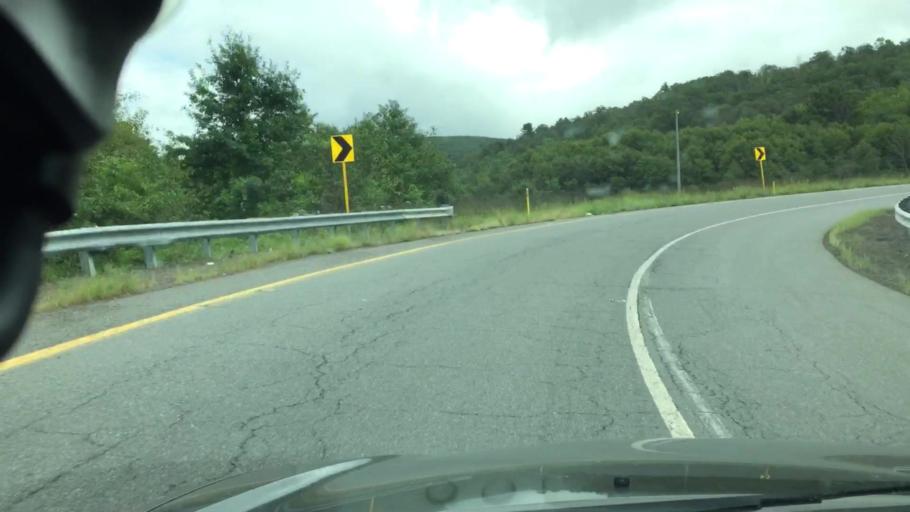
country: US
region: Pennsylvania
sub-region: Luzerne County
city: Ashley
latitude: 41.2017
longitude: -75.9085
